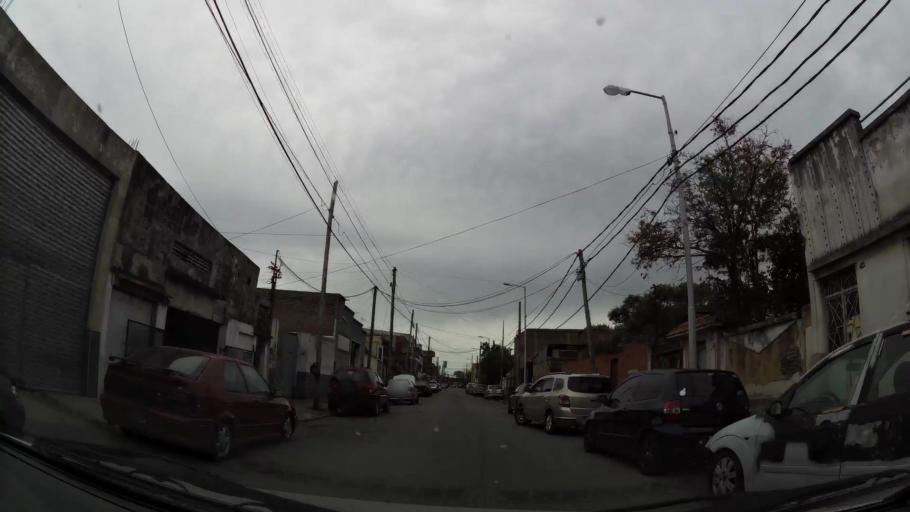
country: AR
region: Buenos Aires
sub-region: Partido de Avellaneda
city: Avellaneda
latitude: -34.6625
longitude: -58.3530
